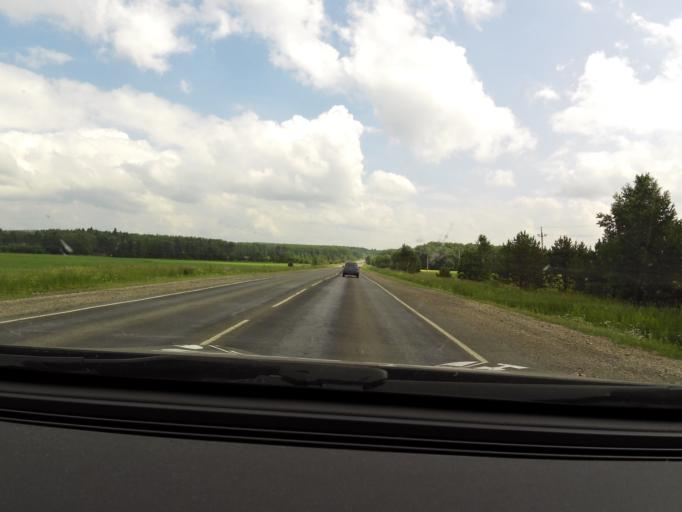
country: RU
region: Sverdlovsk
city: Achit
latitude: 56.8565
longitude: 57.7076
